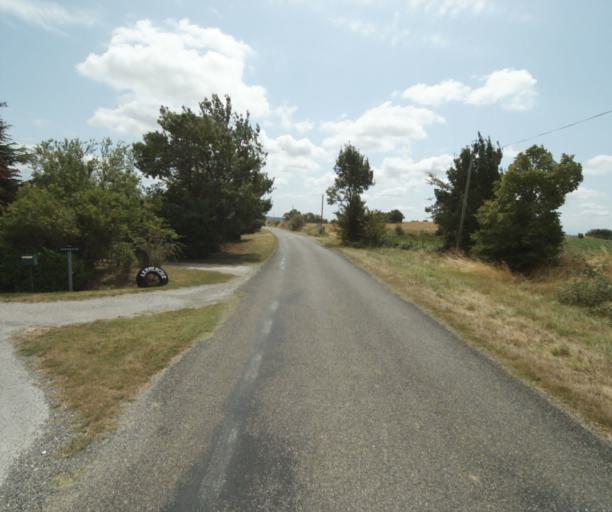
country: FR
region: Midi-Pyrenees
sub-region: Departement de la Haute-Garonne
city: Saint-Felix-Lauragais
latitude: 43.4429
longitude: 1.8926
